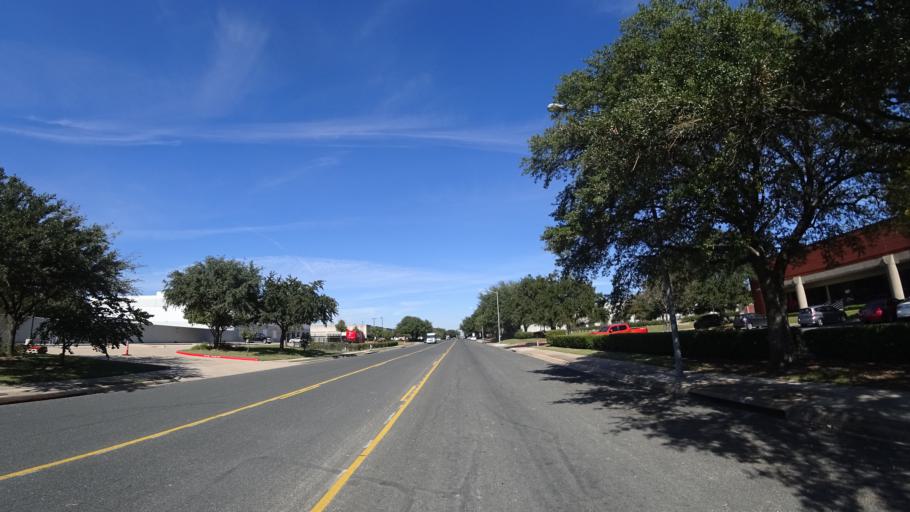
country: US
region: Texas
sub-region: Travis County
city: Austin
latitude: 30.2103
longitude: -97.7434
